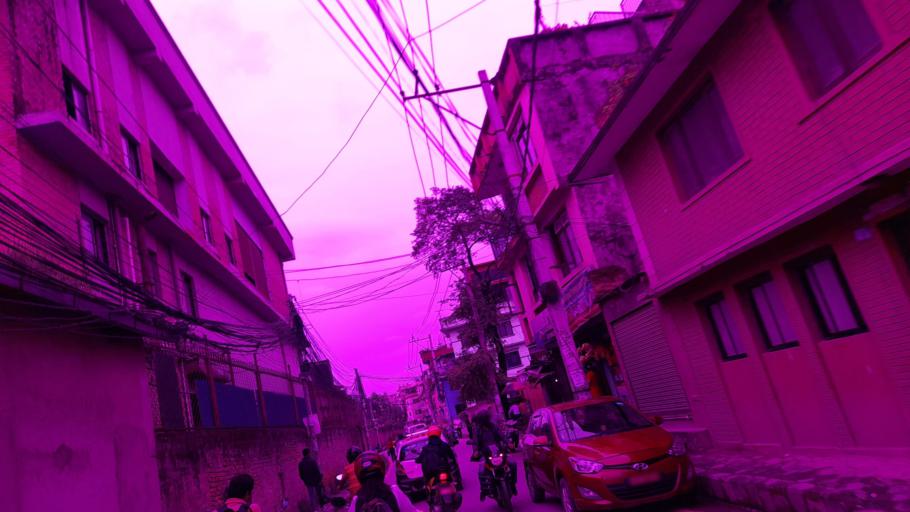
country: NP
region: Central Region
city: Kirtipur
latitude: 27.7013
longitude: 85.2919
